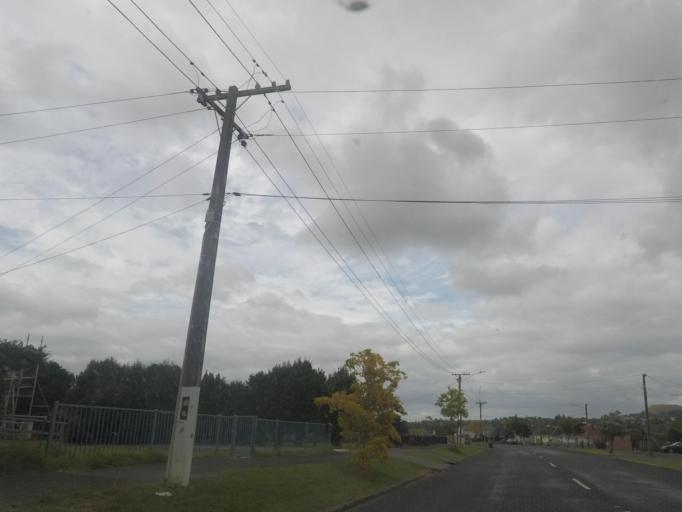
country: NZ
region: Auckland
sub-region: Auckland
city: Tamaki
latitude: -36.8727
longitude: 174.8747
